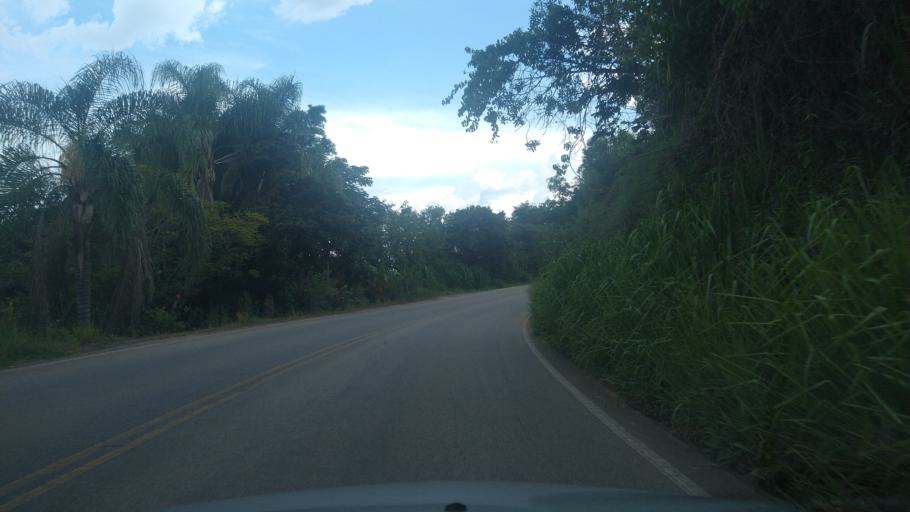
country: BR
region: Minas Gerais
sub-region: Extrema
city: Extrema
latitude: -22.7926
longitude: -46.3173
